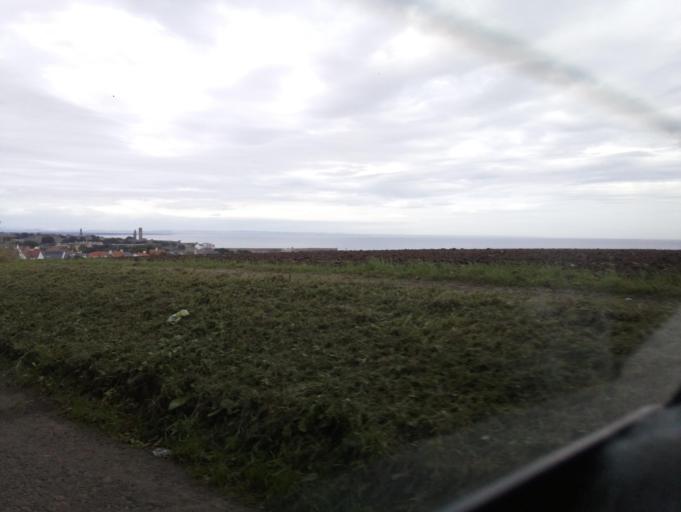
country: GB
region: Scotland
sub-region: Fife
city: Saint Andrews
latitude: 56.3285
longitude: -2.7827
